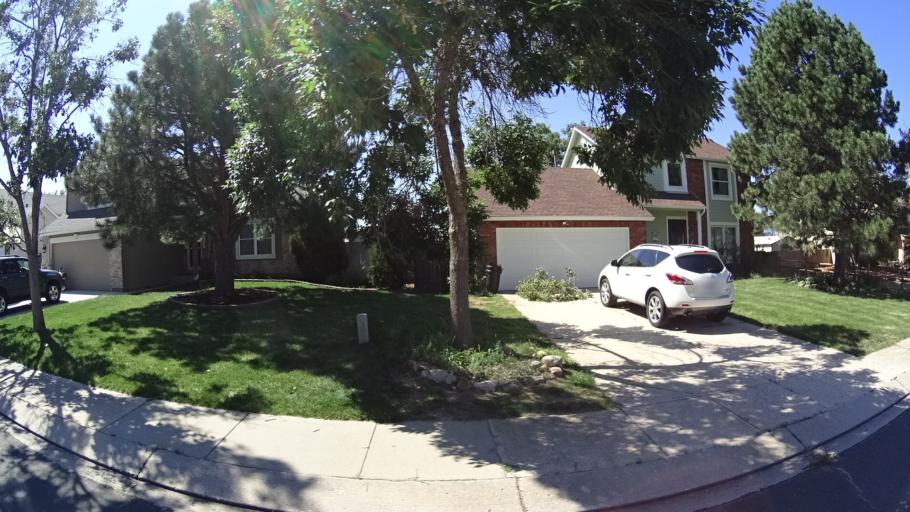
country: US
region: Colorado
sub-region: El Paso County
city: Black Forest
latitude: 38.9370
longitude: -104.7648
